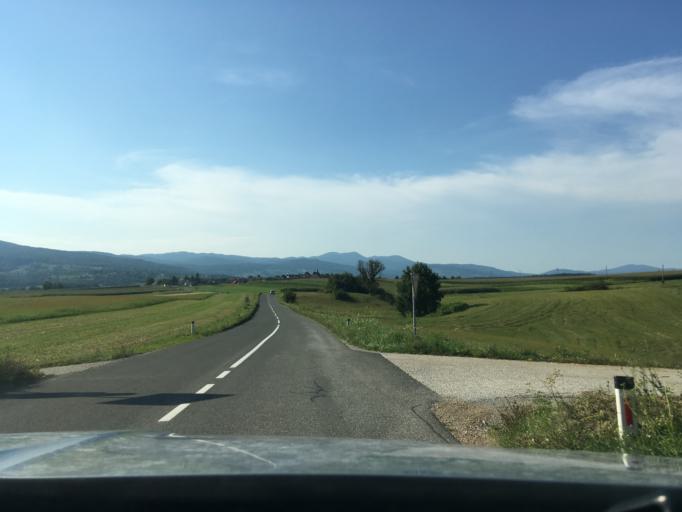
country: SI
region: Crnomelj
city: Crnomelj
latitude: 45.5129
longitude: 15.1847
